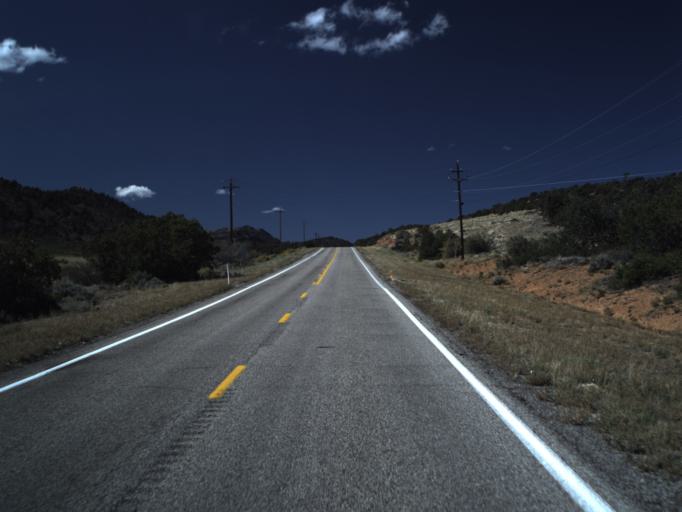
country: US
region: Utah
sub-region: Iron County
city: Cedar City
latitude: 37.6231
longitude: -113.3220
